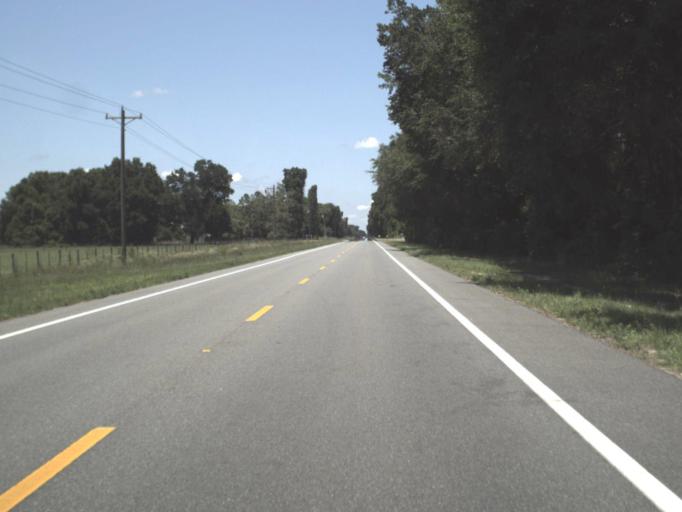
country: US
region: Florida
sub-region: Dixie County
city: Cross City
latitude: 29.7637
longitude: -82.9811
